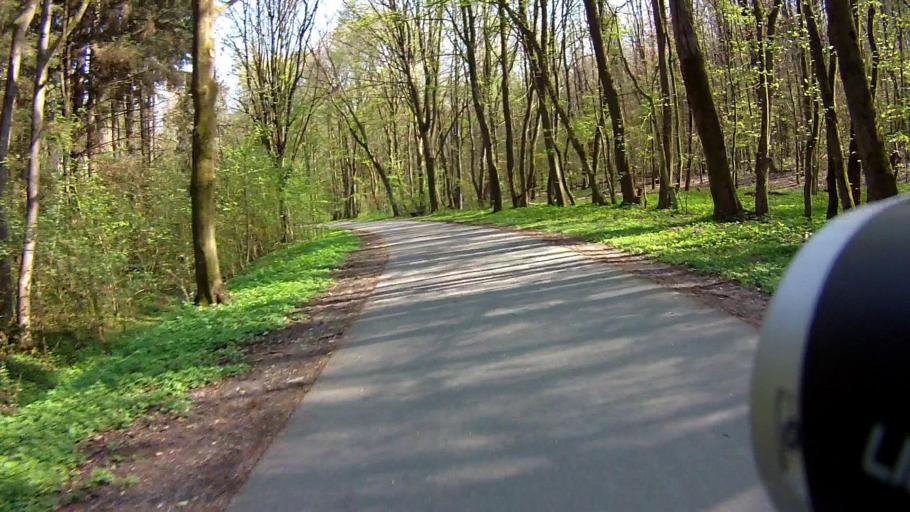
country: DE
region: North Rhine-Westphalia
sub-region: Regierungsbezirk Detmold
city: Paderborn
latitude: 51.7063
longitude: 8.7971
